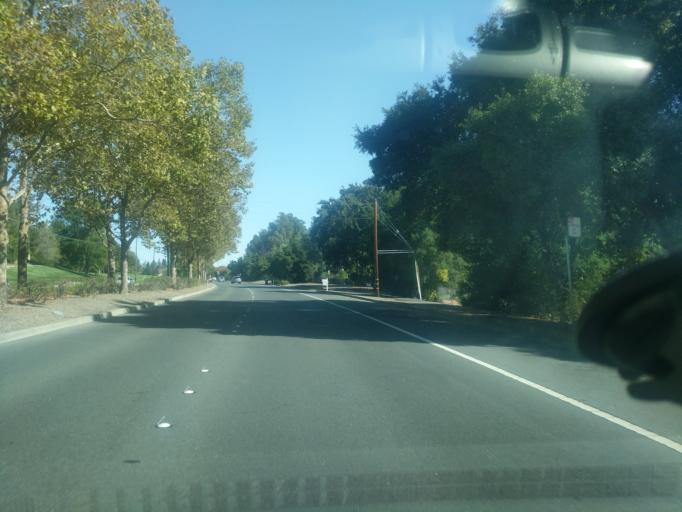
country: US
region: California
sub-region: Contra Costa County
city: Diablo
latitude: 37.8036
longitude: -121.9411
